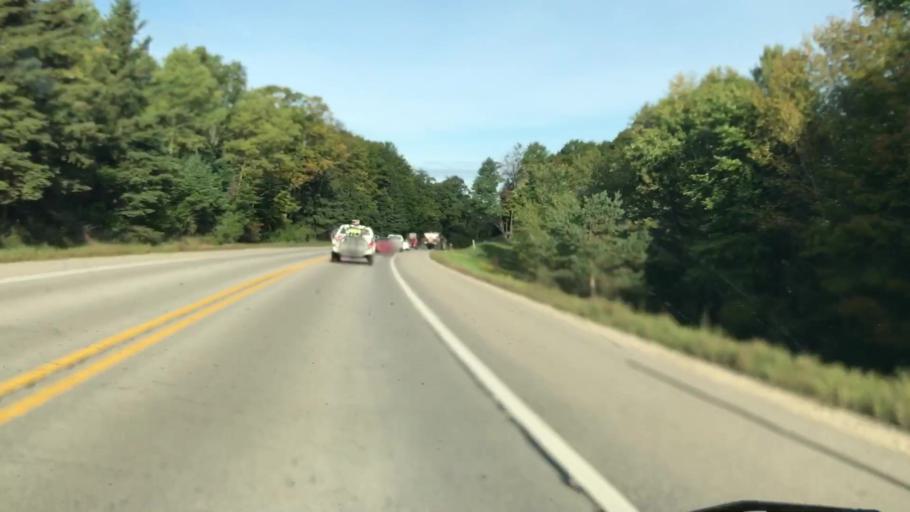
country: US
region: Michigan
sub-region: Luce County
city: Newberry
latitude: 46.3046
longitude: -85.5161
